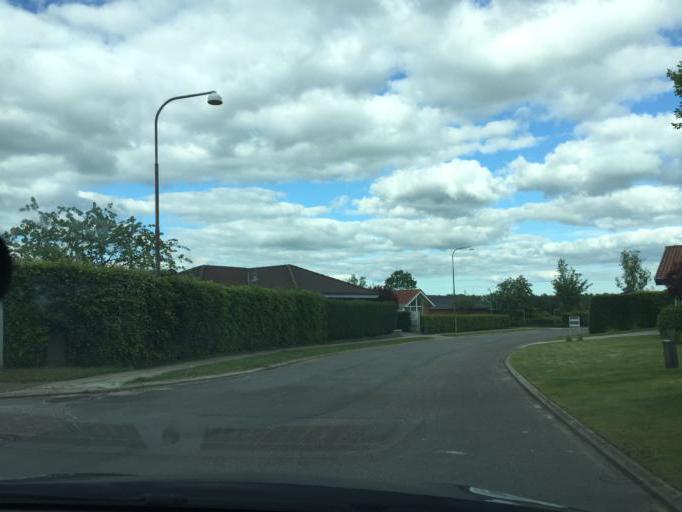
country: DK
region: South Denmark
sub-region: Odense Kommune
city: Bellinge
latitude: 55.3536
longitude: 10.3535
